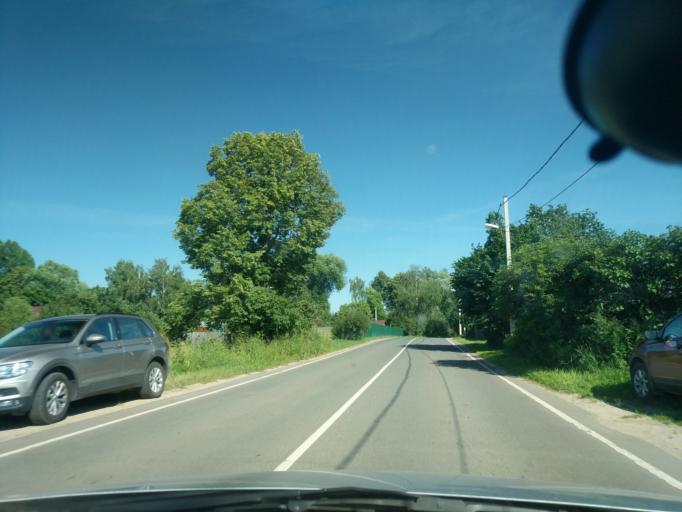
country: RU
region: Moskovskaya
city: Danki
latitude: 54.8455
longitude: 37.5064
